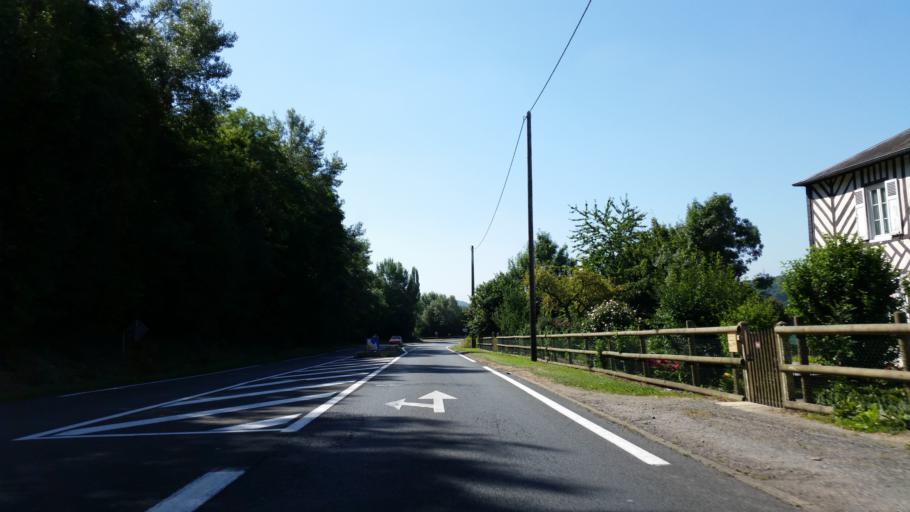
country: FR
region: Lower Normandy
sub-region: Departement du Calvados
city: Lisieux
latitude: 49.2393
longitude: 0.2222
